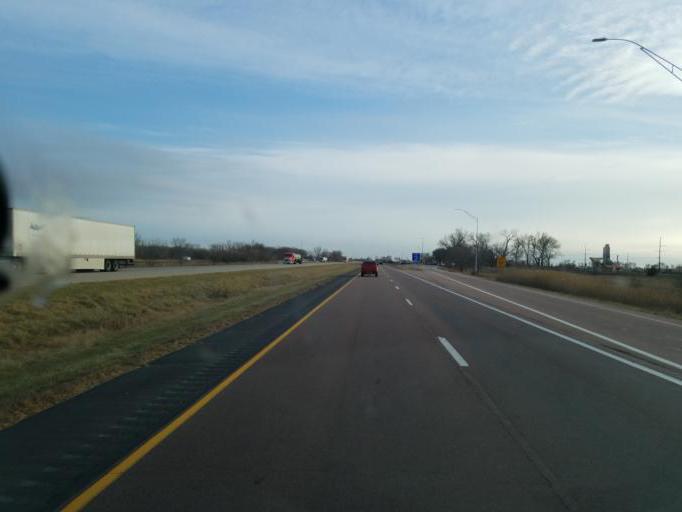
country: US
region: Iowa
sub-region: Woodbury County
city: Sergeant Bluff
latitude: 42.3786
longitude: -96.3564
